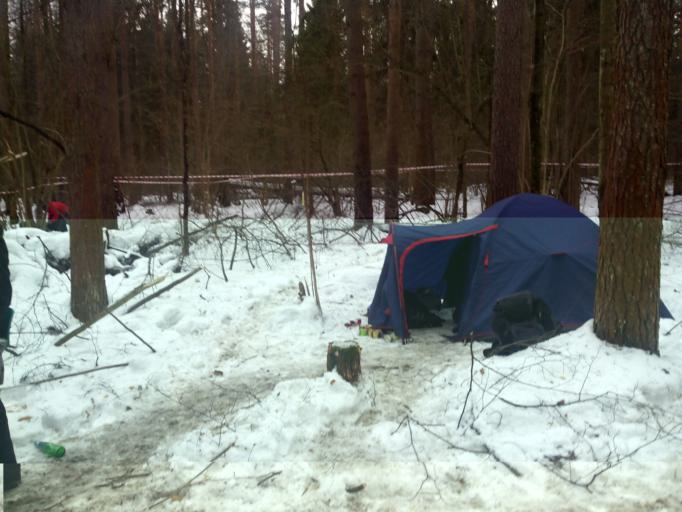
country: RU
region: Moskovskaya
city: Bol'shiye Vyazemy
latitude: 55.6614
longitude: 36.9897
